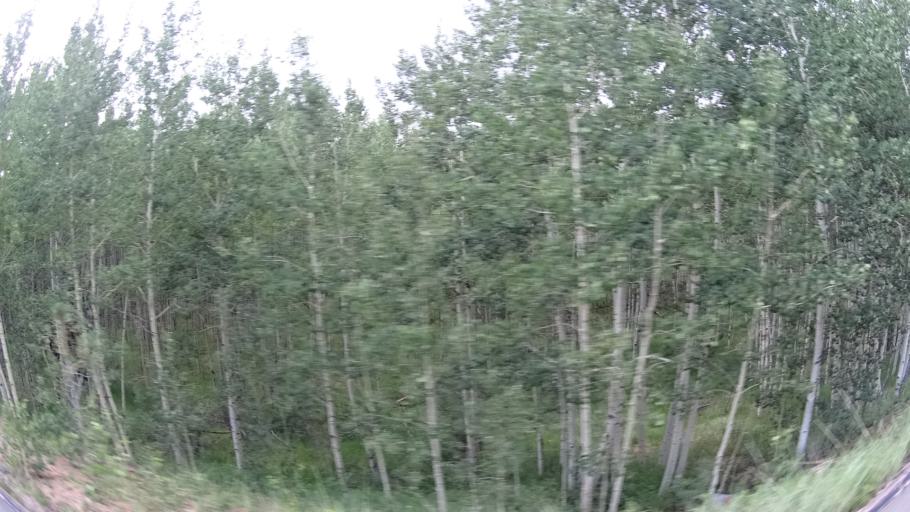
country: US
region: Colorado
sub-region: El Paso County
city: Cascade-Chipita Park
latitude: 38.9104
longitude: -105.0183
